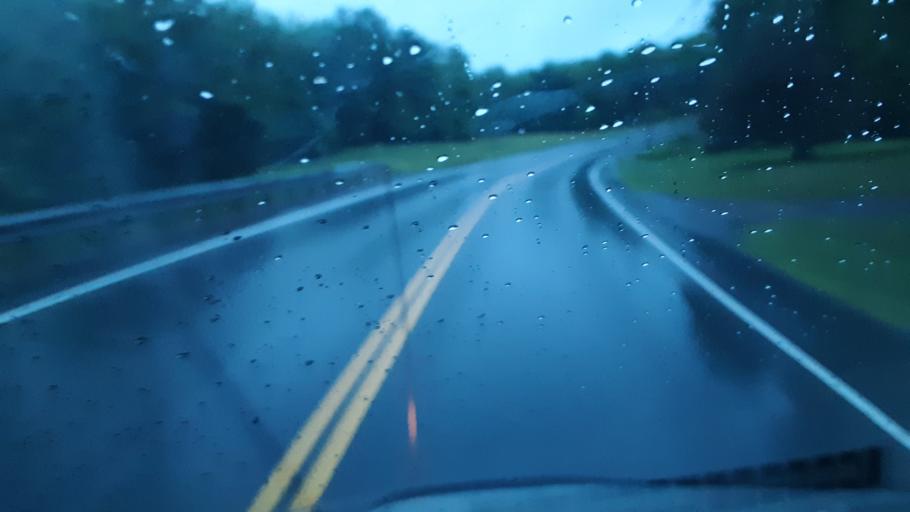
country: US
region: Maine
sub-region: Penobscot County
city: Patten
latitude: 45.8854
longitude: -68.4183
